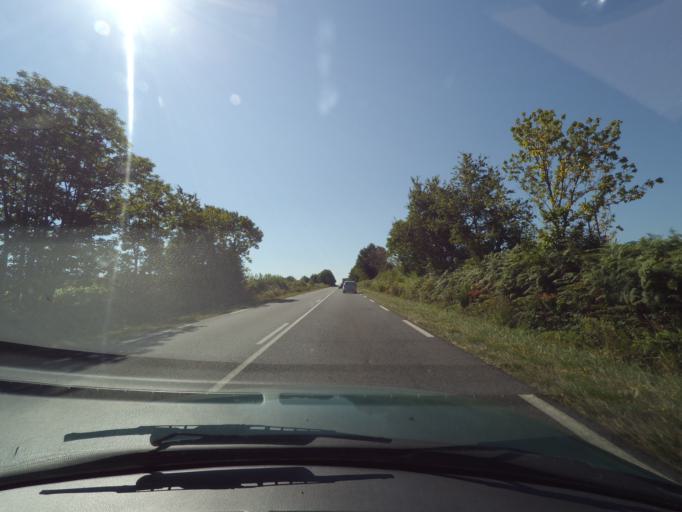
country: FR
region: Limousin
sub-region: Departement de la Haute-Vienne
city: Bussiere-Poitevine
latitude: 46.1893
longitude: 0.9304
